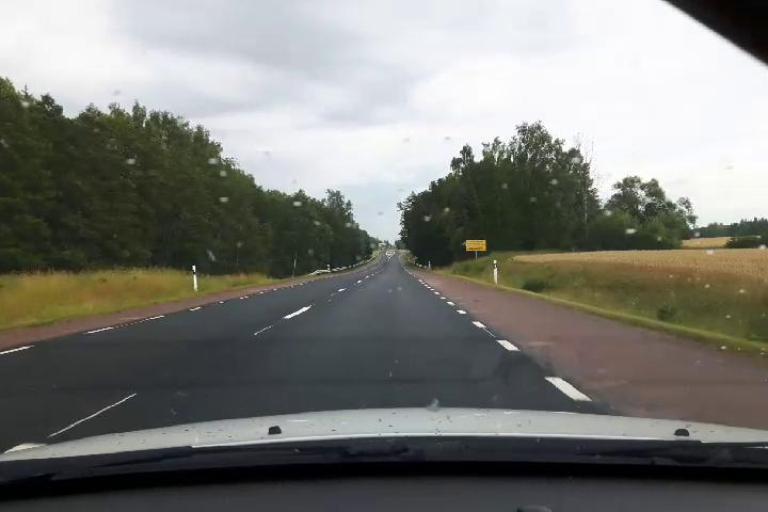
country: SE
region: Uppsala
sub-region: Uppsala Kommun
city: Gamla Uppsala
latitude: 59.9584
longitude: 17.5844
